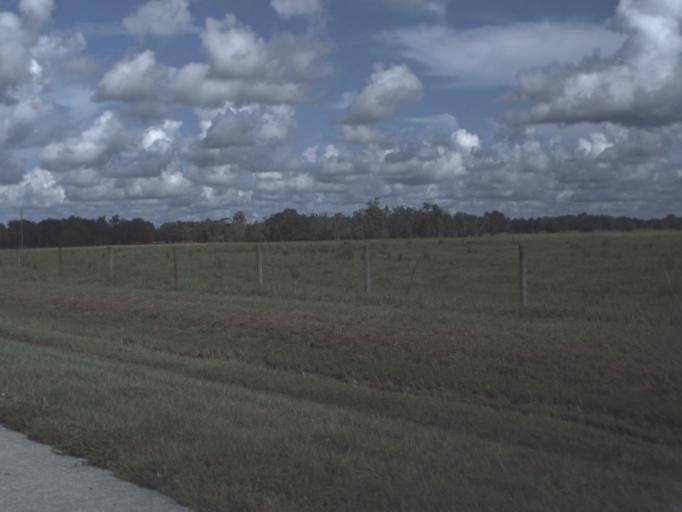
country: US
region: Florida
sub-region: DeSoto County
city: Arcadia
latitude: 27.2486
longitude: -81.9540
